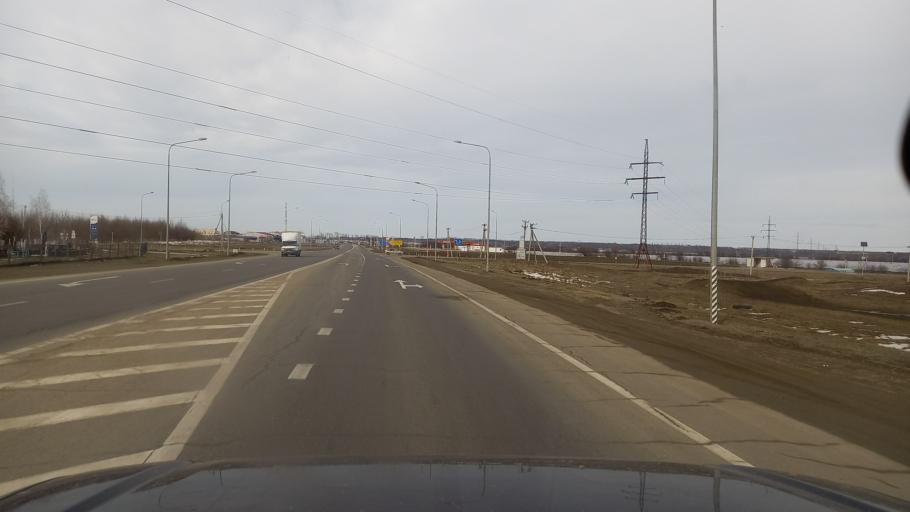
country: RU
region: Krasnodarskiy
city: Belorechensk
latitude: 44.7675
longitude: 39.9119
